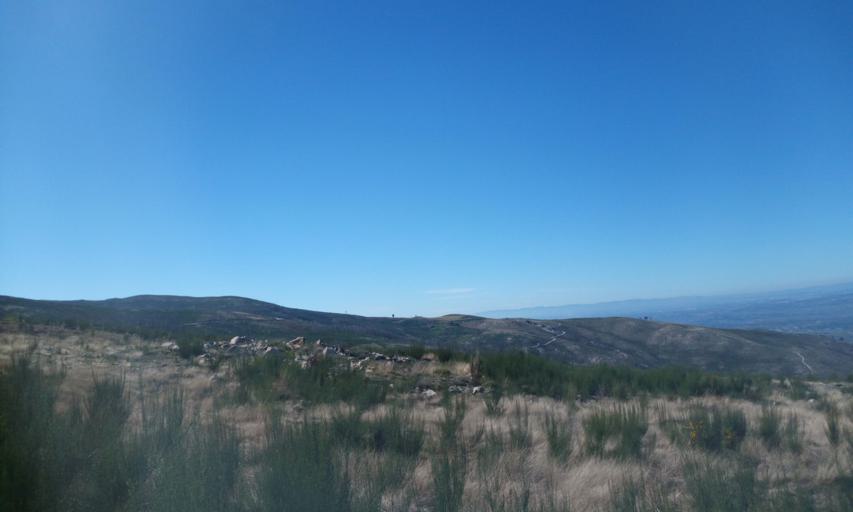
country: PT
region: Guarda
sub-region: Manteigas
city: Manteigas
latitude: 40.4989
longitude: -7.5209
